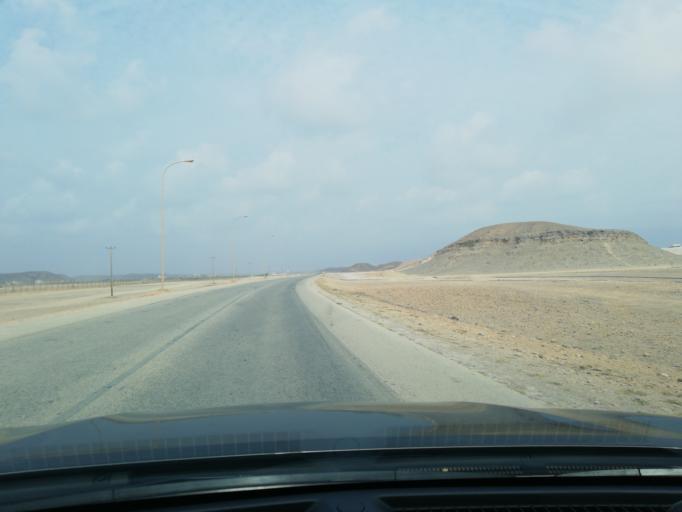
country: OM
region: Zufar
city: Salalah
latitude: 16.9461
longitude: 53.9490
